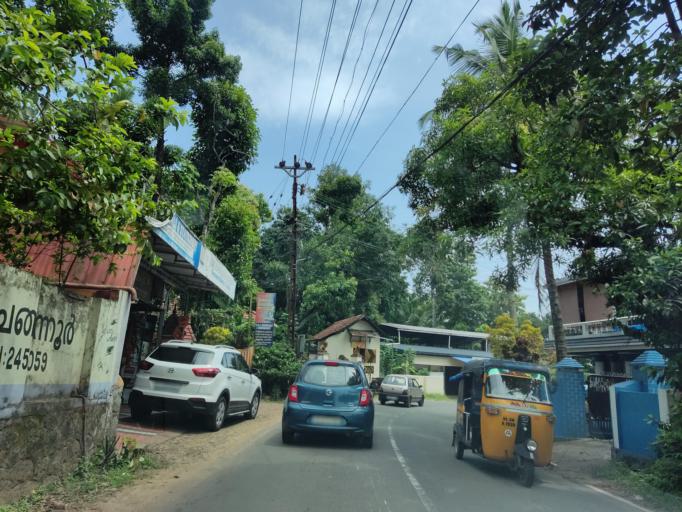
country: IN
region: Kerala
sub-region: Alappuzha
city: Chengannur
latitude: 9.3117
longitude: 76.6039
